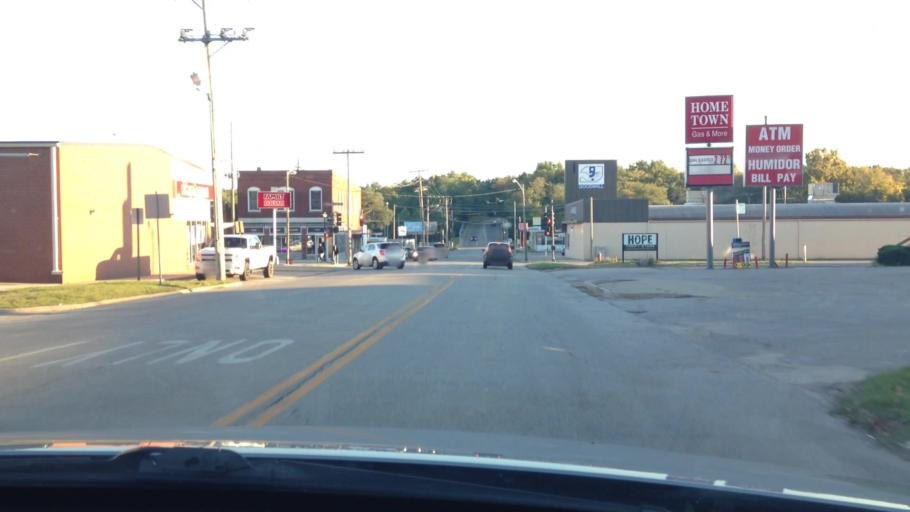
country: US
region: Kansas
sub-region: Leavenworth County
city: Leavenworth
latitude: 39.3189
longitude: -94.9216
